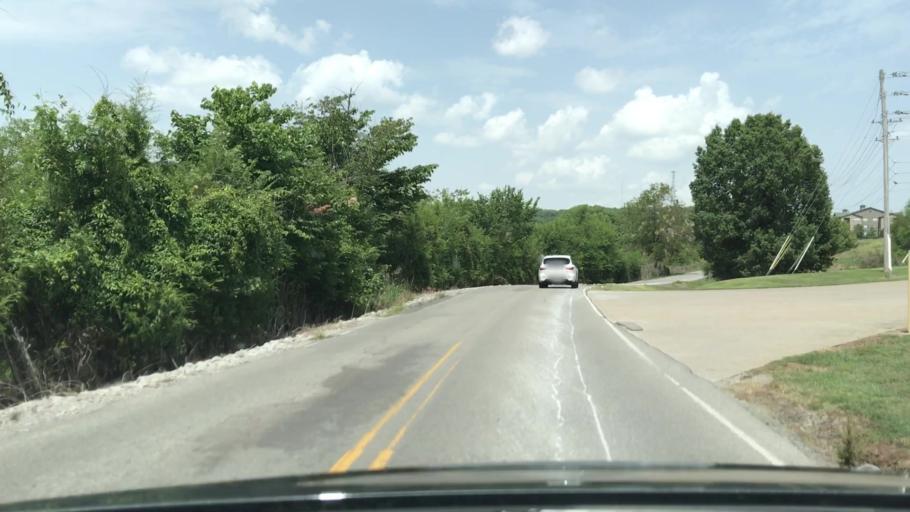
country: US
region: Tennessee
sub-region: Rutherford County
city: La Vergne
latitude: 35.9714
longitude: -86.5791
